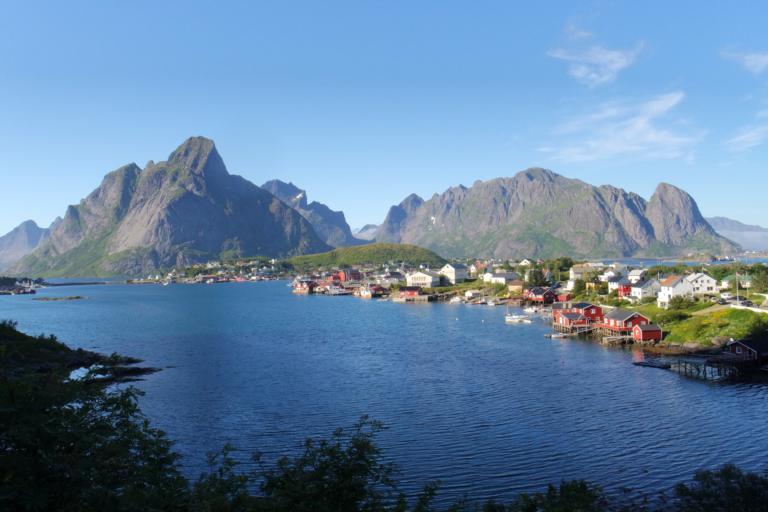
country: NO
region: Nordland
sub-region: Moskenes
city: Reine
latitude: 67.9284
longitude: 13.0845
